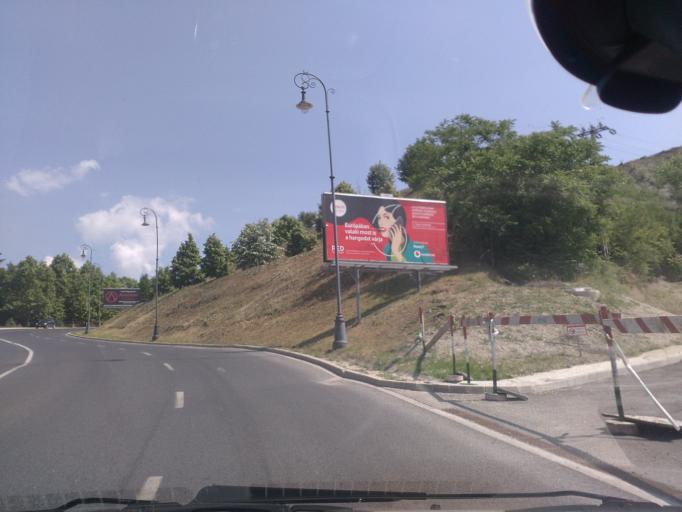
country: HU
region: Komarom-Esztergom
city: Esztergom
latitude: 47.7963
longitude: 18.7450
